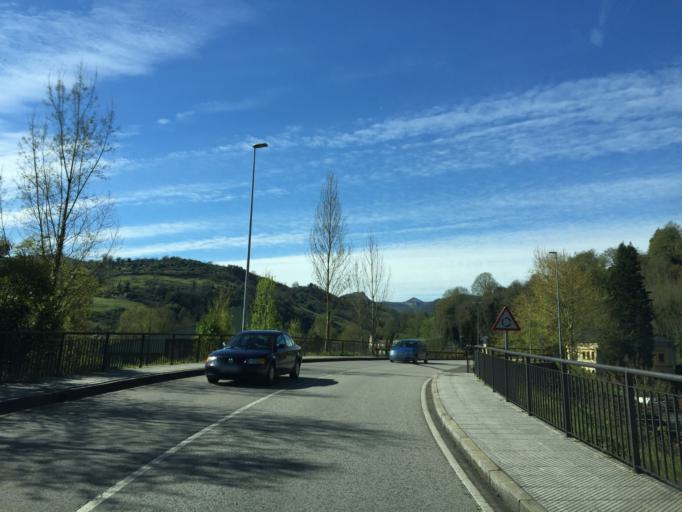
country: ES
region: Asturias
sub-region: Province of Asturias
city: Castandiello
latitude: 43.3529
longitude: -5.9673
